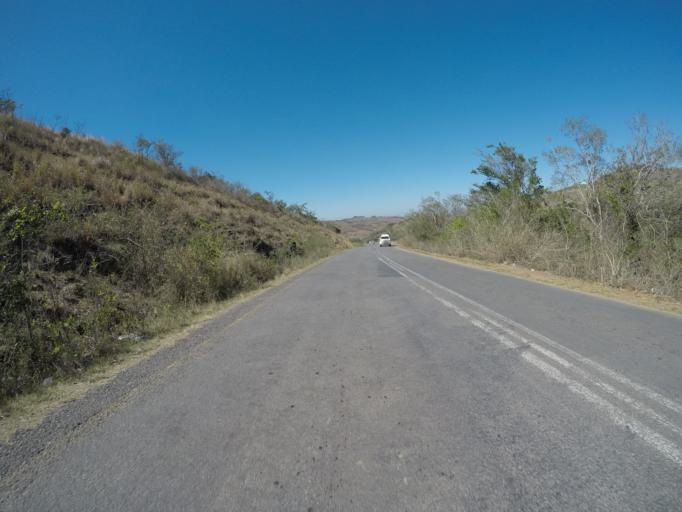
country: ZA
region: Eastern Cape
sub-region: OR Tambo District Municipality
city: Mthatha
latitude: -31.9122
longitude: 28.9610
